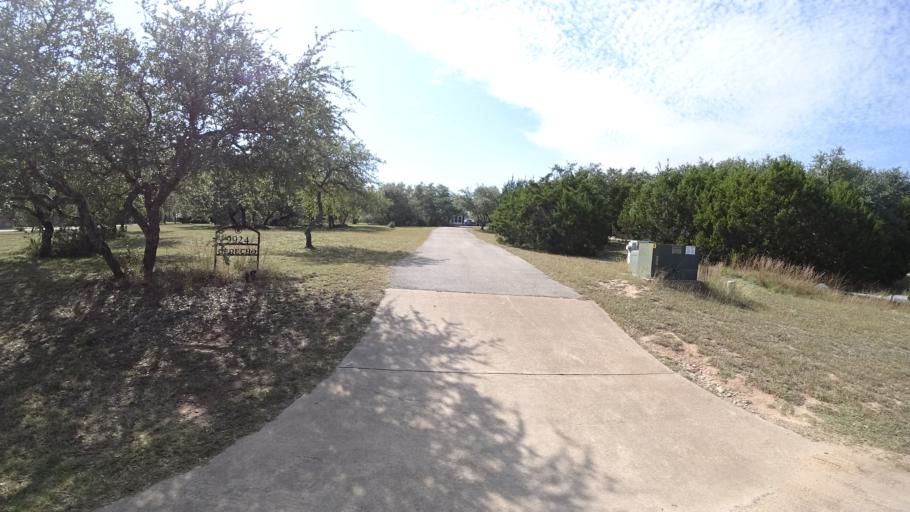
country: US
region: Texas
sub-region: Travis County
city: Bee Cave
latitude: 30.2265
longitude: -97.9371
